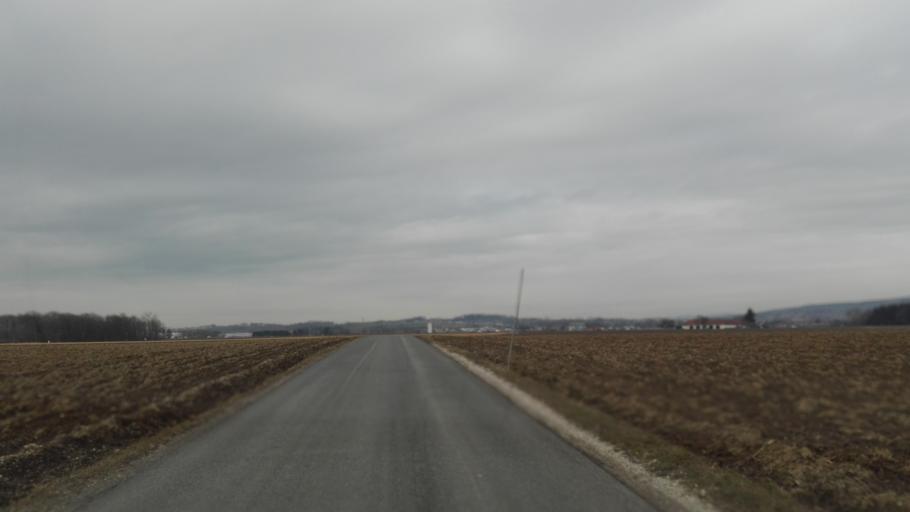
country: AT
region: Upper Austria
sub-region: Politischer Bezirk Linz-Land
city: Traun
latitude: 48.2372
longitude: 14.2136
